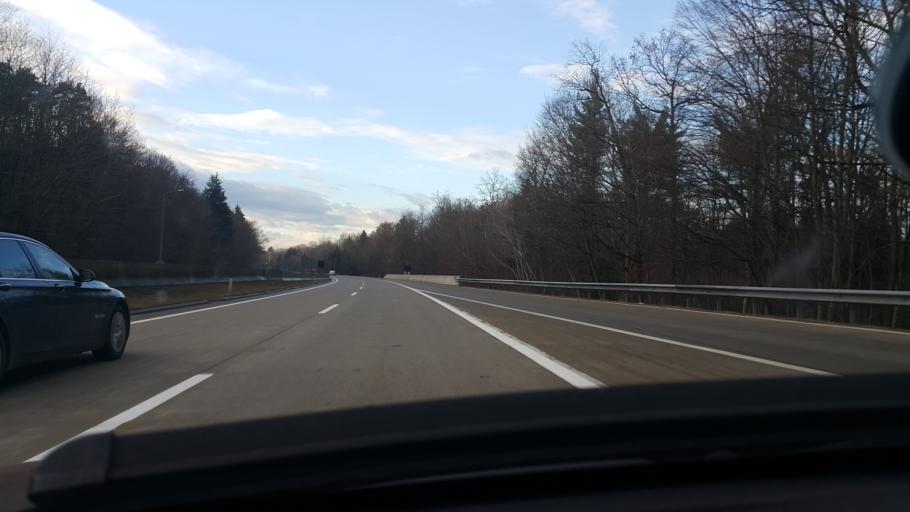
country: AT
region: Styria
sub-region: Politischer Bezirk Leibnitz
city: Strass in Steiermark
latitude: 46.7343
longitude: 15.6381
